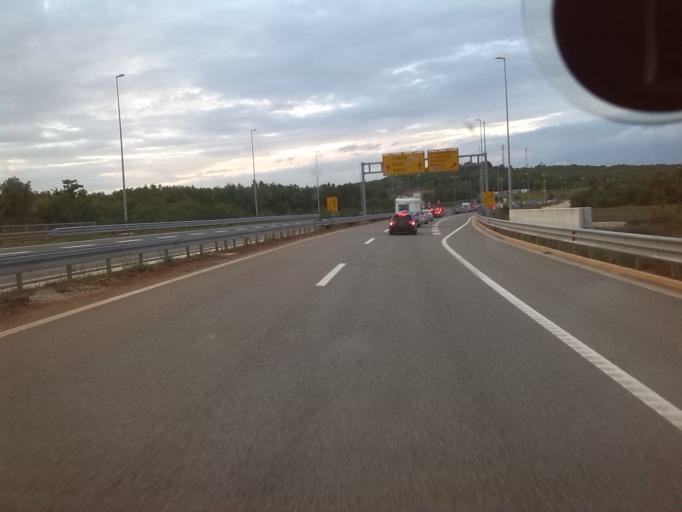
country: SI
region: Piran-Pirano
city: Seca
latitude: 45.4485
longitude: 13.6177
